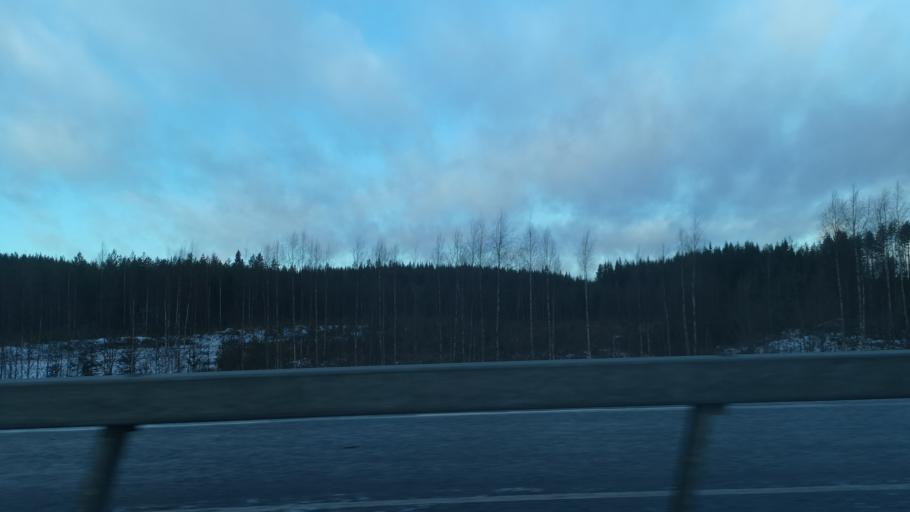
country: FI
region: Southern Savonia
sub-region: Mikkeli
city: Maentyharju
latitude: 61.5060
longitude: 26.7982
